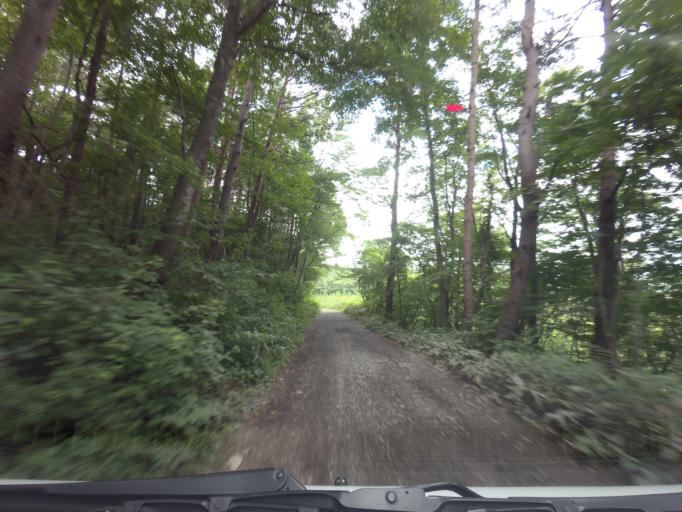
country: JP
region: Fukushima
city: Nihommatsu
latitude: 37.6005
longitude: 140.3449
